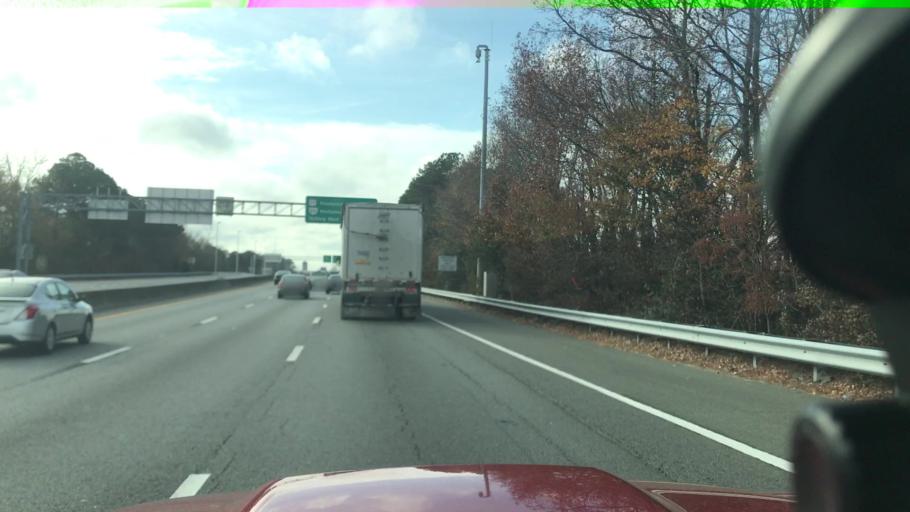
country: US
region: Virginia
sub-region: City of Portsmouth
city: Portsmouth
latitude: 36.8293
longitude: -76.3158
